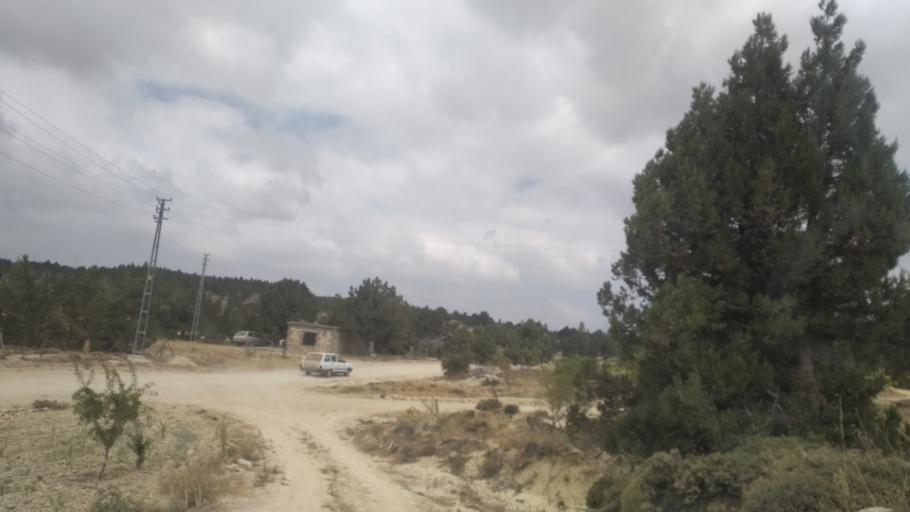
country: TR
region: Mersin
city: Sarikavak
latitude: 36.5682
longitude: 33.7652
